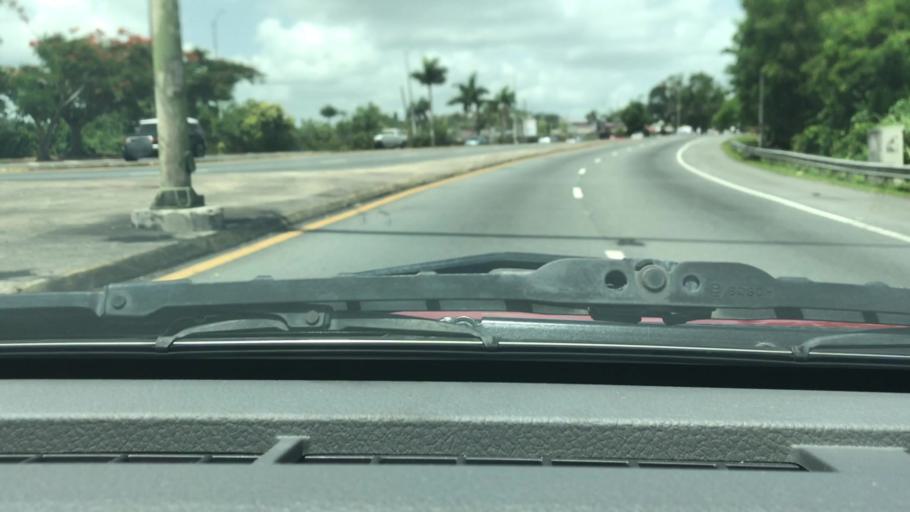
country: PR
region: Bayamon
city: Bayamon
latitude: 18.3665
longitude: -66.1681
